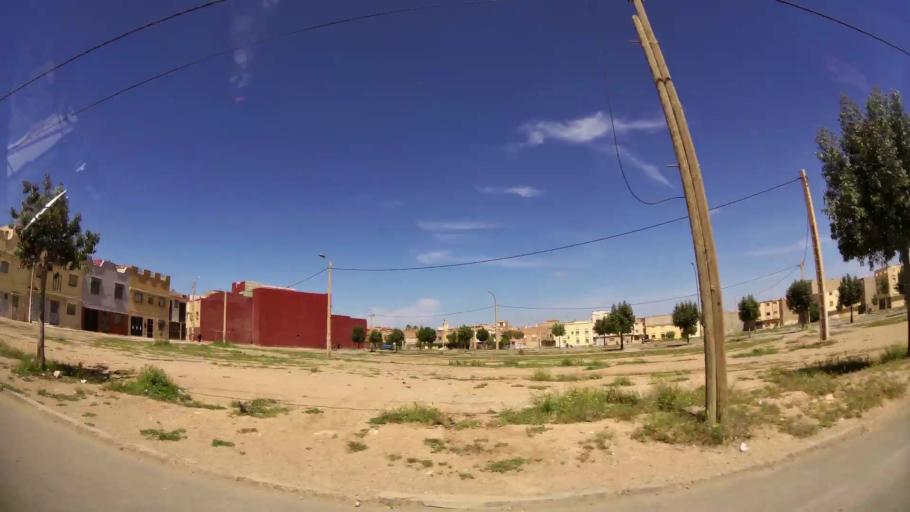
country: MA
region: Oriental
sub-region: Oujda-Angad
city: Oujda
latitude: 34.6657
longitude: -1.9274
